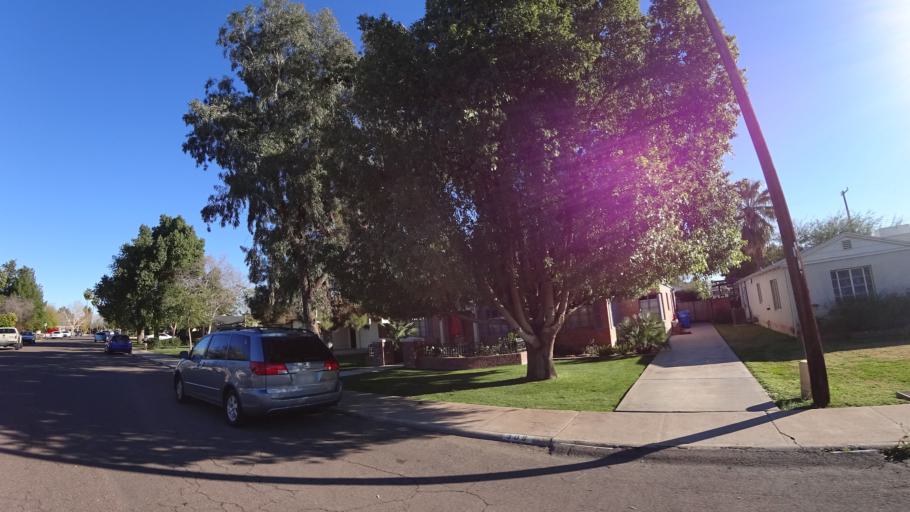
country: US
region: Arizona
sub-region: Maricopa County
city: Phoenix
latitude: 33.5120
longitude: -112.0690
